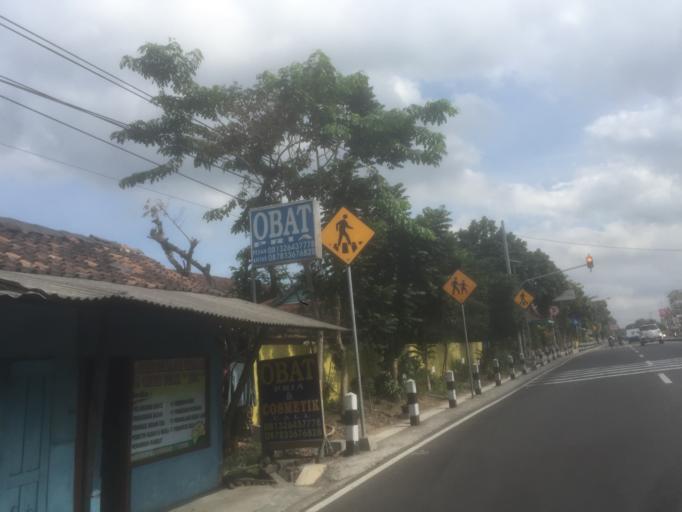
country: ID
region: Daerah Istimewa Yogyakarta
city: Sleman
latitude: -7.6908
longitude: 110.3433
